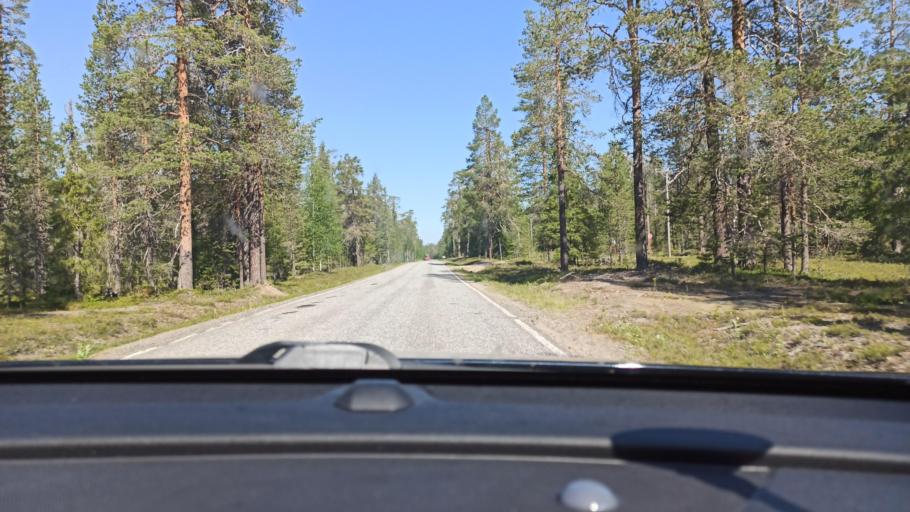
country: FI
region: Lapland
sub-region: Tunturi-Lappi
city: Kolari
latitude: 67.6621
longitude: 24.1647
